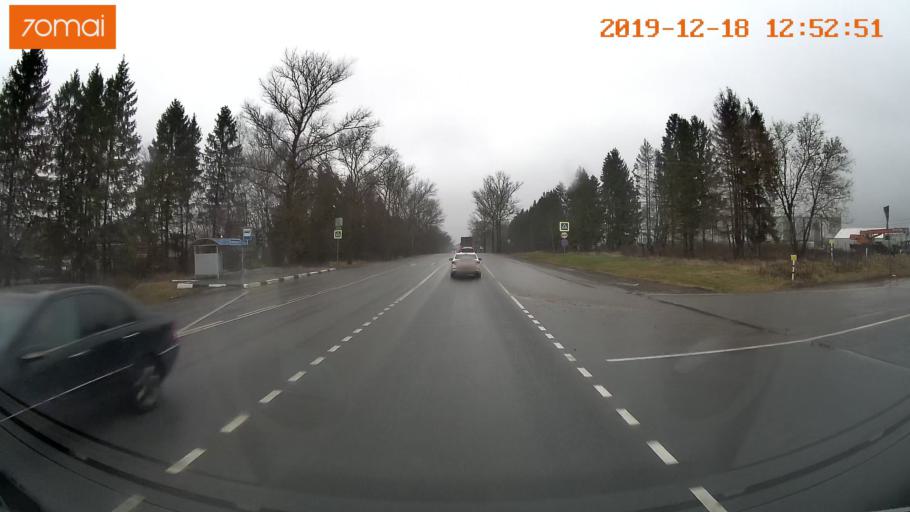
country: RU
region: Moskovskaya
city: Klin
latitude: 56.3145
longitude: 36.6902
